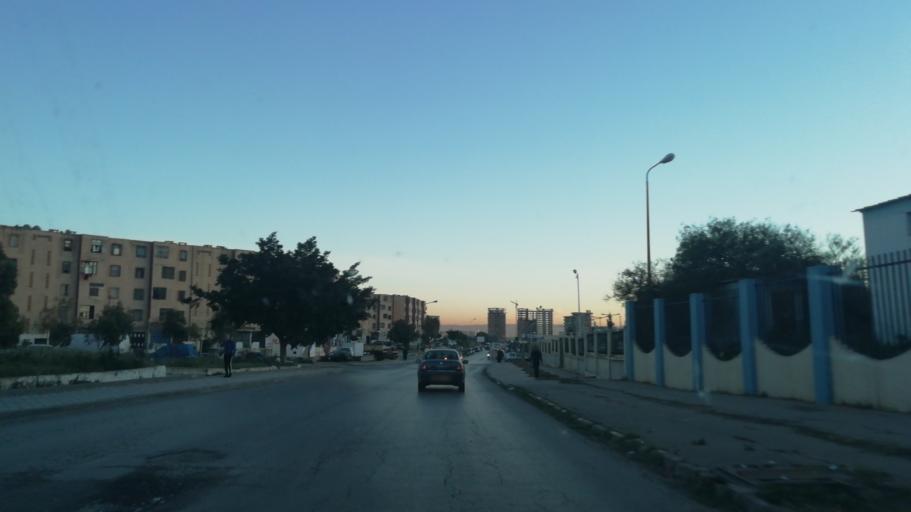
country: DZ
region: Oran
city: Bir el Djir
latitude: 35.7064
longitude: -0.5910
